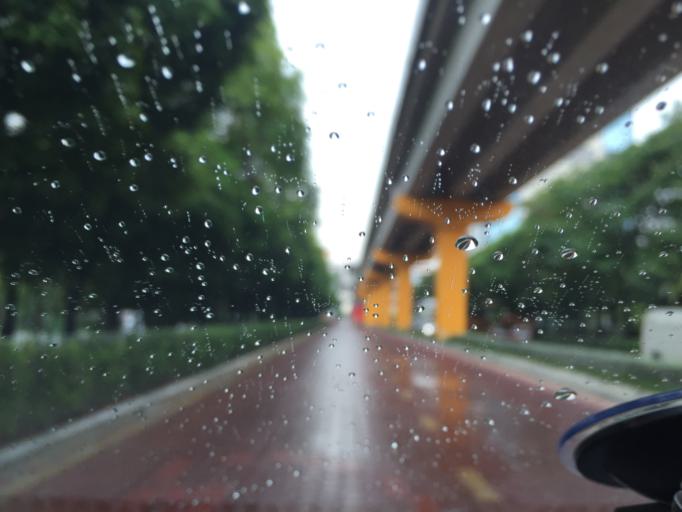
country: MY
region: Selangor
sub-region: Petaling
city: Petaling Jaya
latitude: 3.0721
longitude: 101.6108
